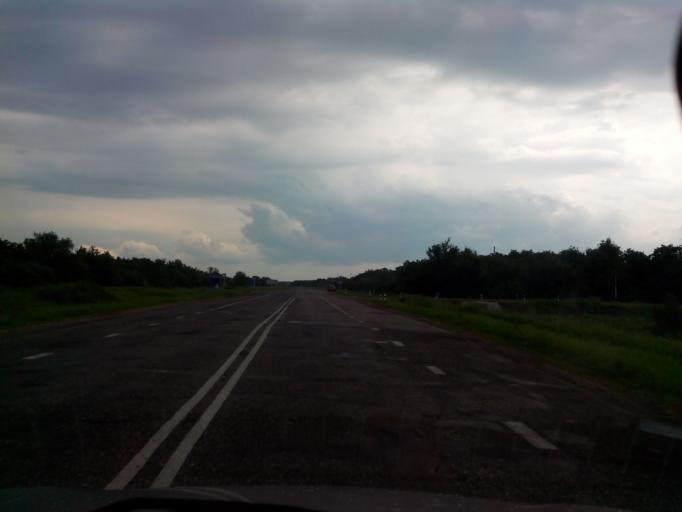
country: RU
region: Volgograd
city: Kumylzhenskaya
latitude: 49.8967
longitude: 42.8238
